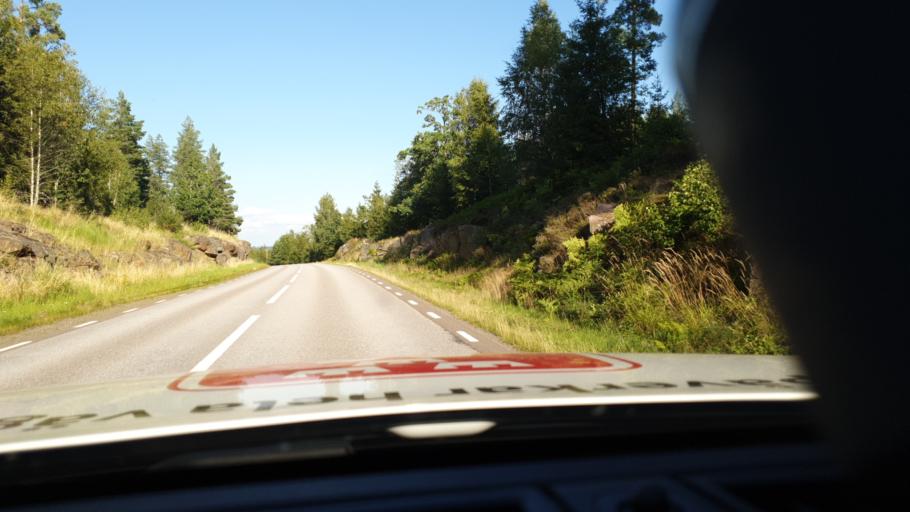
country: SE
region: OEstergoetland
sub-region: Ydre Kommun
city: OEsterbymo
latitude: 57.9188
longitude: 15.4372
